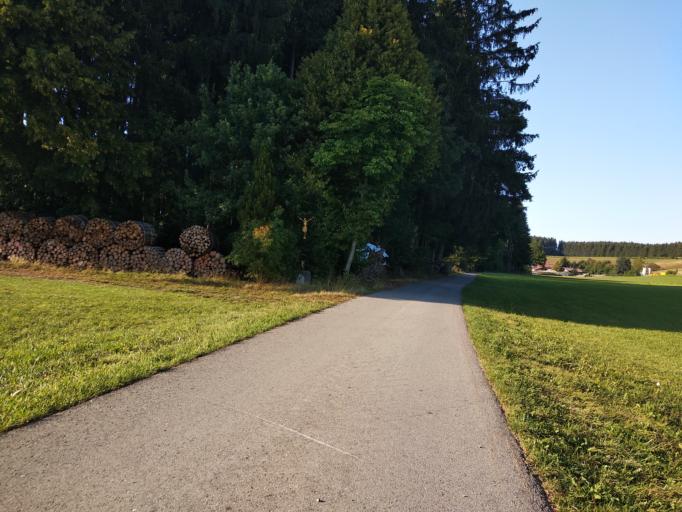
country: DE
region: Bavaria
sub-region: Swabia
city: Legau
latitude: 47.8696
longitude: 10.1068
